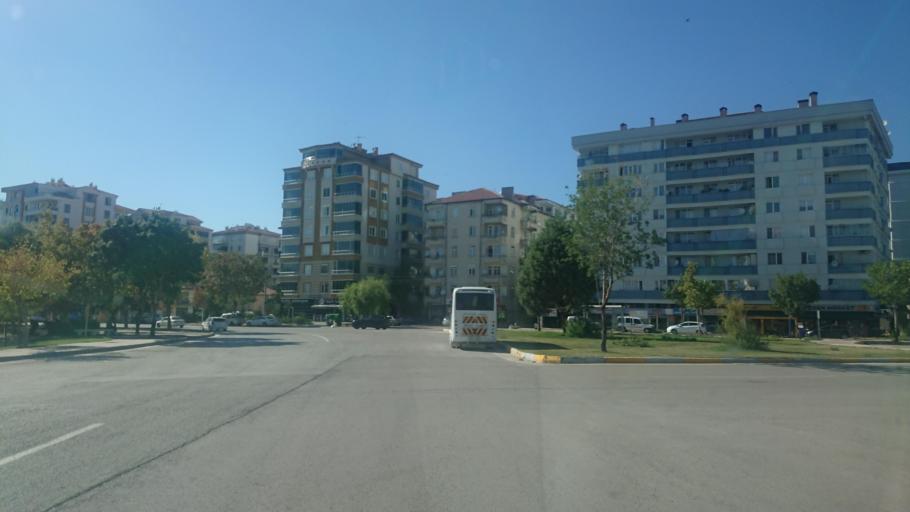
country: TR
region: Aksaray
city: Aksaray
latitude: 38.3645
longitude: 34.0108
